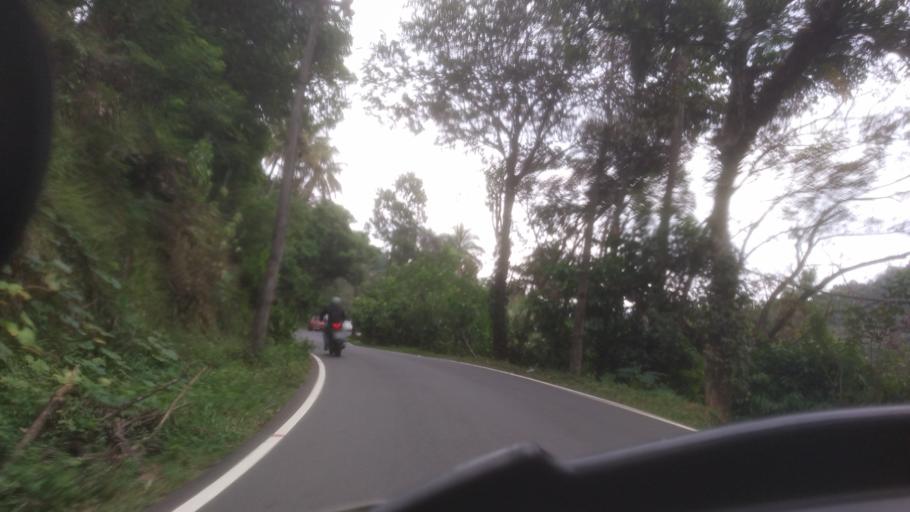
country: IN
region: Kerala
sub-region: Idukki
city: Idukki
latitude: 9.9617
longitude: 77.0052
